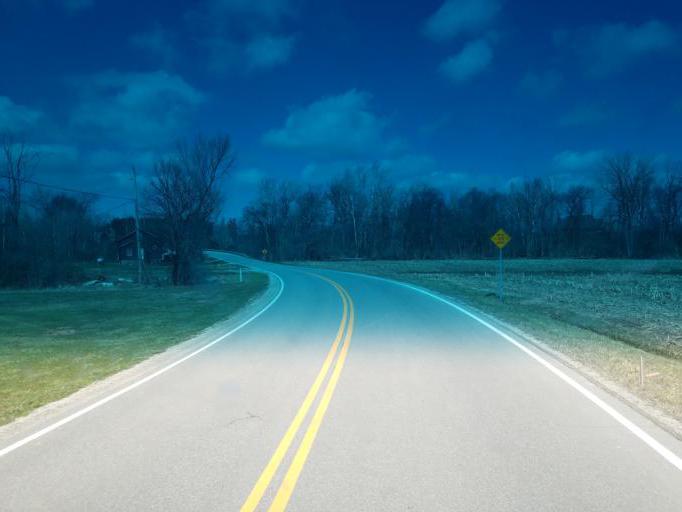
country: US
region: Ohio
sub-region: Crawford County
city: Bucyrus
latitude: 40.8030
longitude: -83.0041
